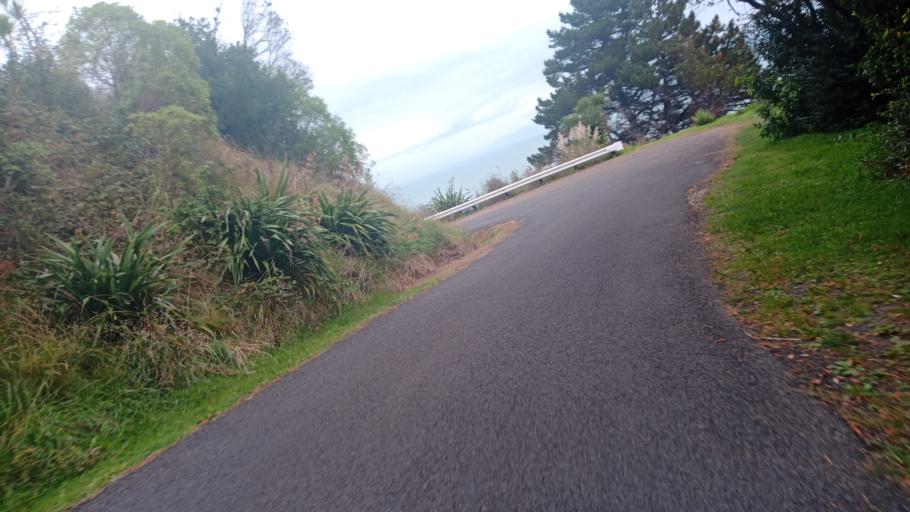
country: NZ
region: Gisborne
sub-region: Gisborne District
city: Gisborne
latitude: -38.6831
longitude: 178.0381
